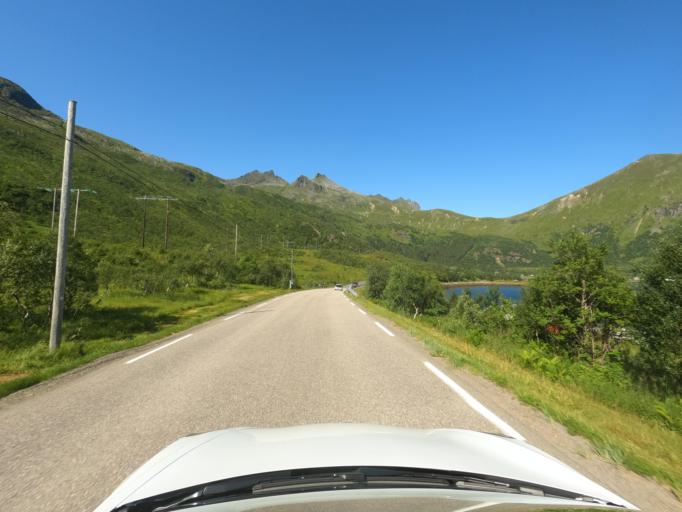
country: NO
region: Nordland
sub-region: Hadsel
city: Melbu
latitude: 68.3511
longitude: 14.7126
